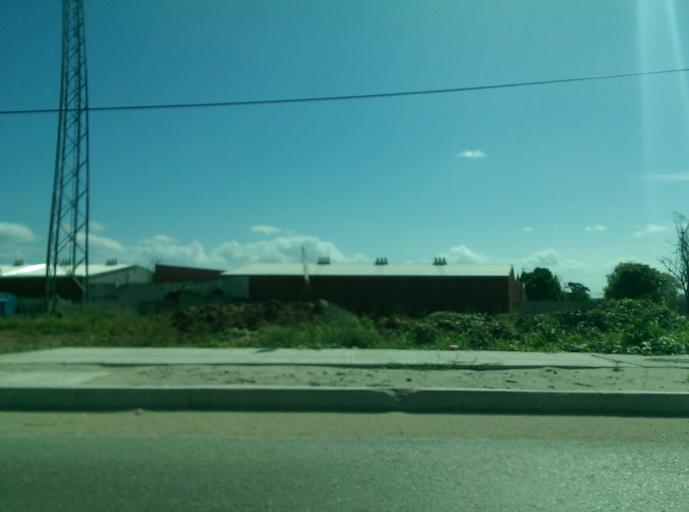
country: MX
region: Tabasco
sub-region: Centro
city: Anacleto Canabal 3ra. Seccion
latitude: 17.9858
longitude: -92.9931
